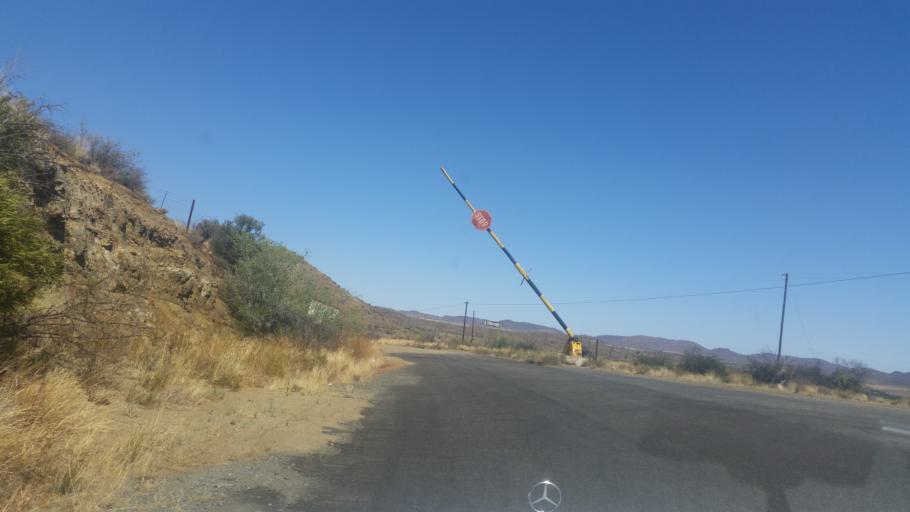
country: ZA
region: Northern Cape
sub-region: Pixley ka Seme District Municipality
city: Colesberg
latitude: -30.6232
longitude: 25.4843
